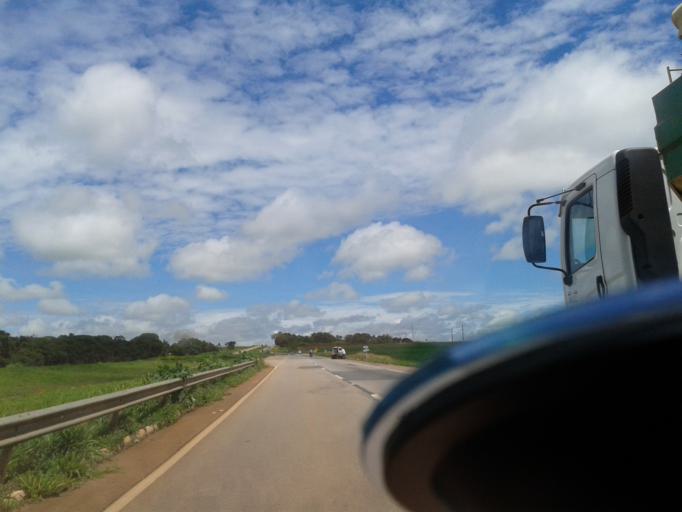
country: BR
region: Goias
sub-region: Inhumas
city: Inhumas
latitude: -16.2646
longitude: -49.5475
